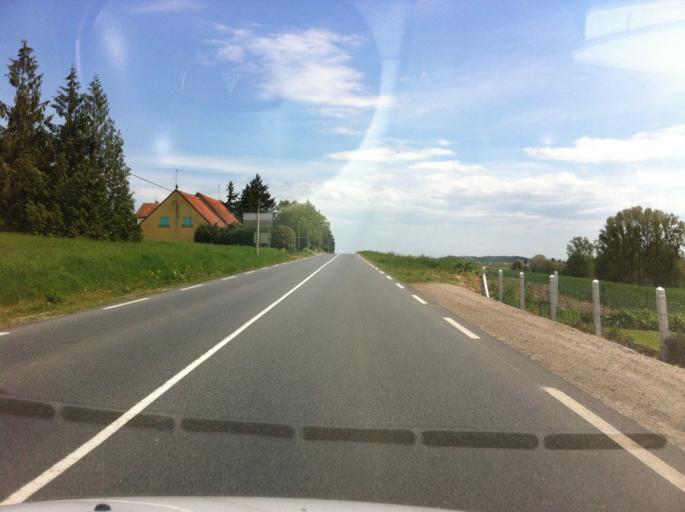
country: FR
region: Auvergne
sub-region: Departement de l'Allier
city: Saint-Pourcain-sur-Sioule
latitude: 46.3143
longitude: 3.2651
